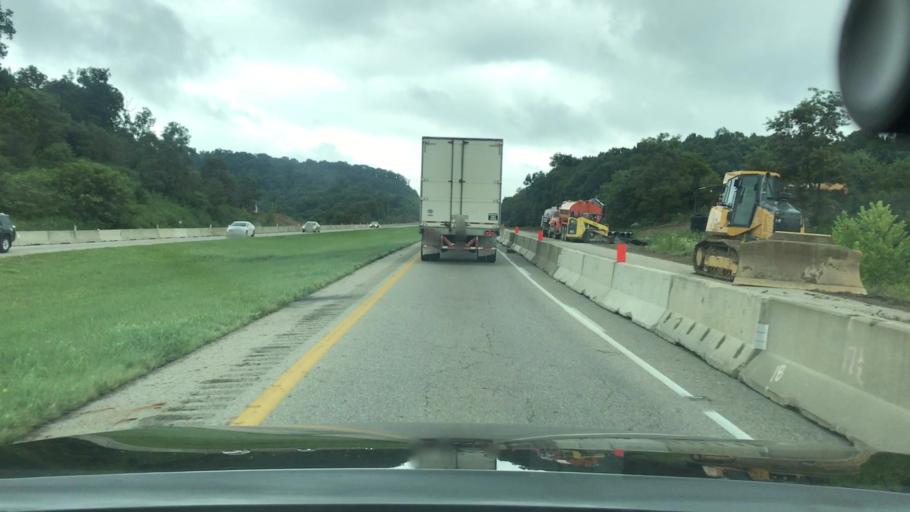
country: US
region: Ohio
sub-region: Ross County
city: Chillicothe
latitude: 39.2393
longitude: -82.8396
